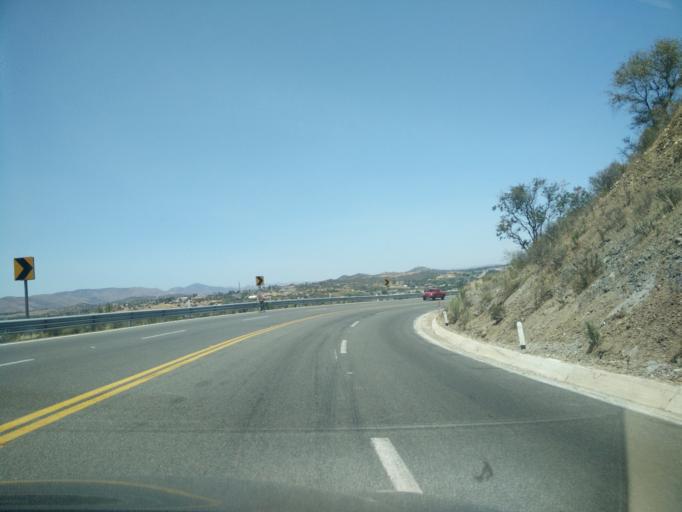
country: MX
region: Baja California
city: El Sauzal
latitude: 31.9621
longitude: -116.6608
